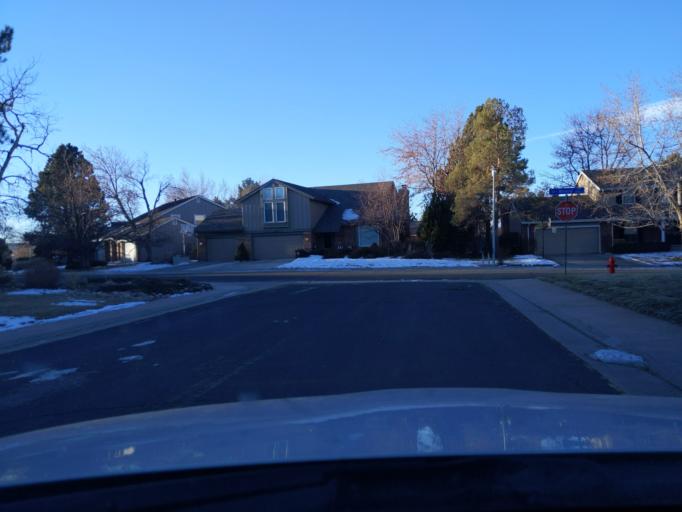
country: US
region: Colorado
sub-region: Arapahoe County
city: Centennial
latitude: 39.5729
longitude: -104.8876
